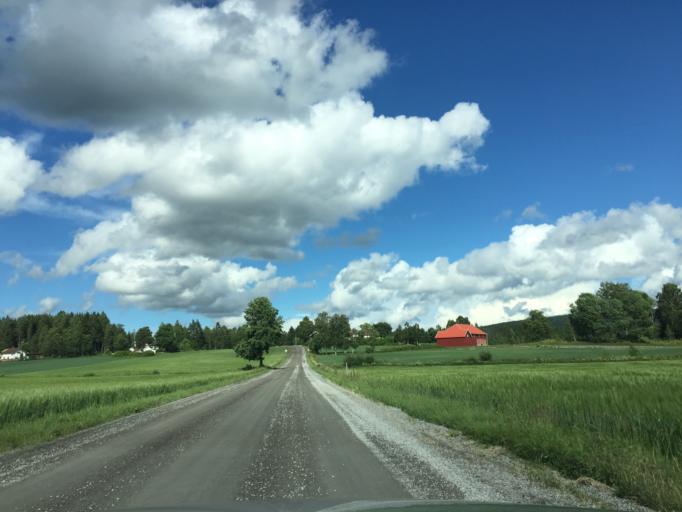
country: NO
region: Hedmark
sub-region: Kongsvinger
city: Spetalen
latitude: 60.2381
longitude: 11.8287
